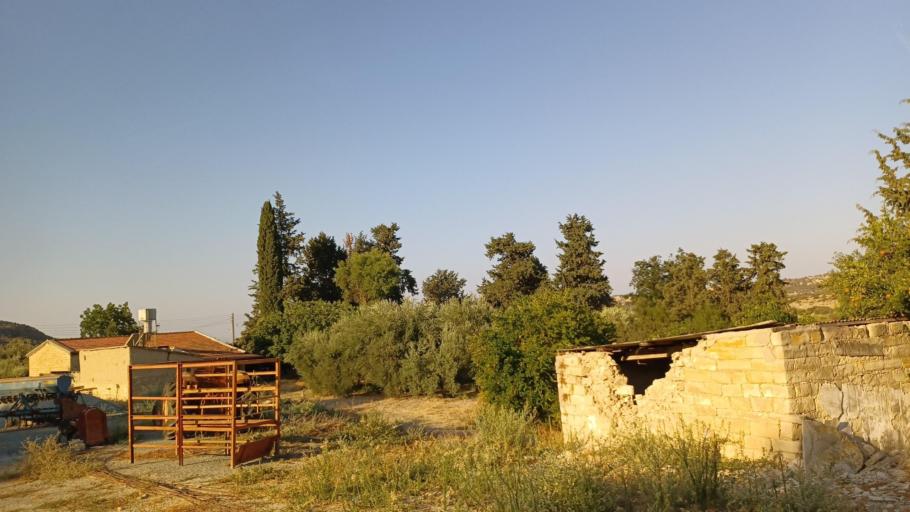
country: CY
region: Limassol
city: Pissouri
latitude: 34.7102
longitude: 32.6817
